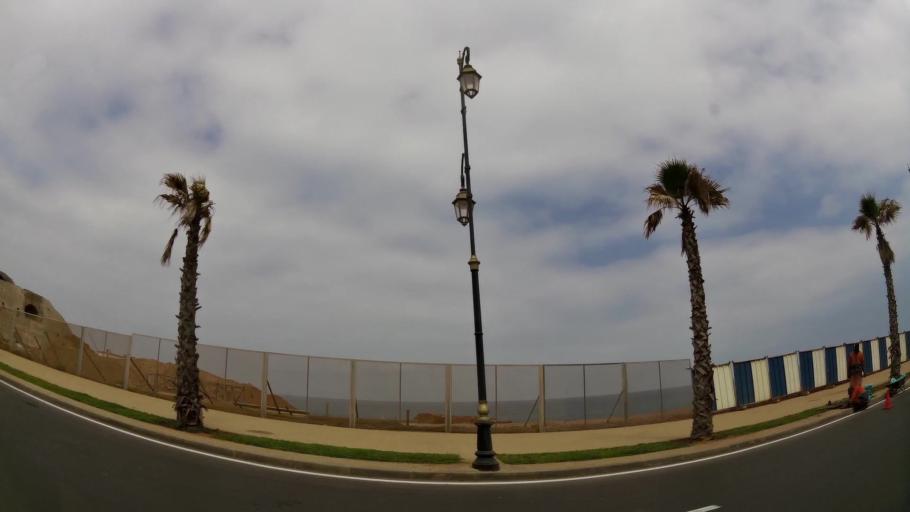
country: MA
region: Rabat-Sale-Zemmour-Zaer
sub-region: Rabat
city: Rabat
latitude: 34.0253
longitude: -6.8502
